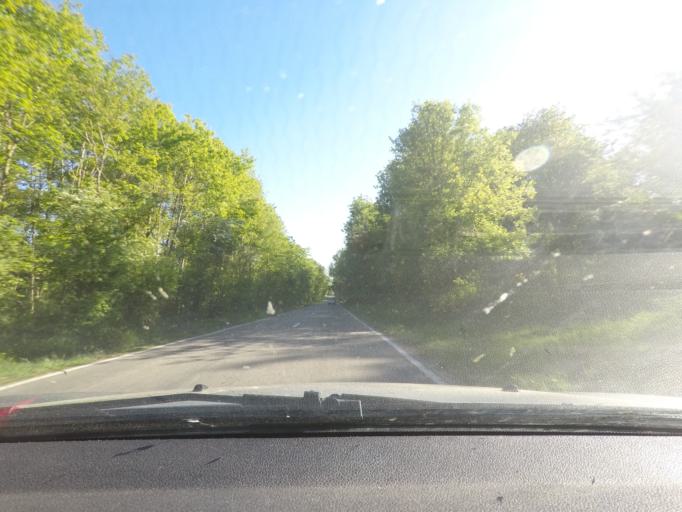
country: BE
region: Wallonia
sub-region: Province du Luxembourg
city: Wellin
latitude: 50.1808
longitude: 5.1205
